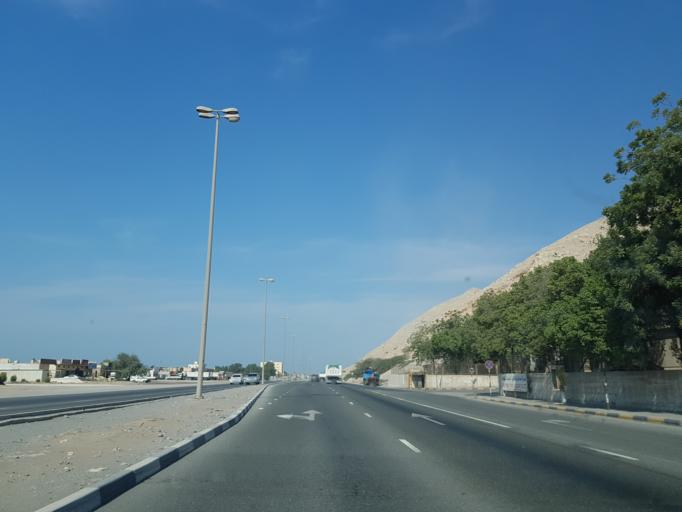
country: AE
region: Ra's al Khaymah
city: Ras al-Khaimah
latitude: 25.8576
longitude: 56.0208
